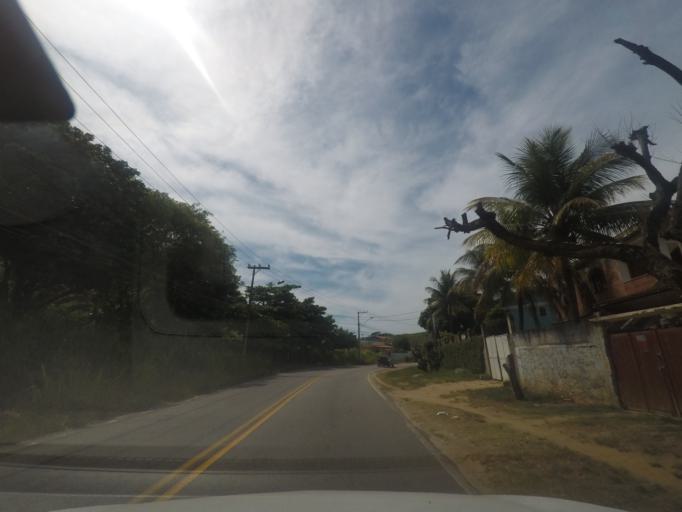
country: BR
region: Rio de Janeiro
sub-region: Marica
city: Marica
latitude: -22.9468
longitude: -42.6980
